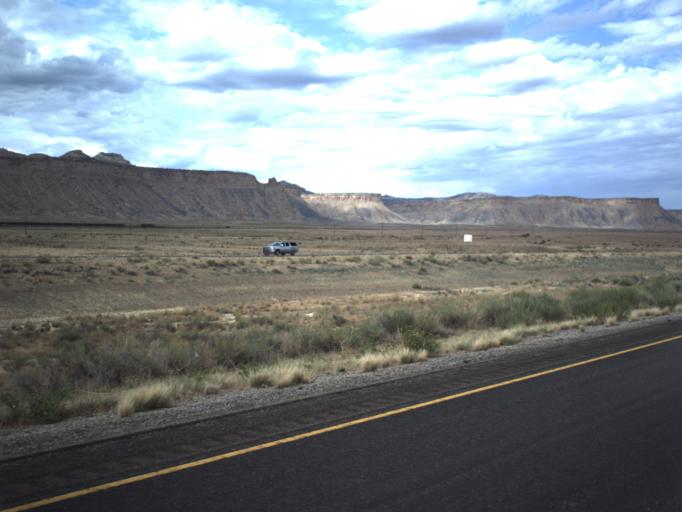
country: US
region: Utah
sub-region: Grand County
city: Moab
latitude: 38.9450
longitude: -109.7982
